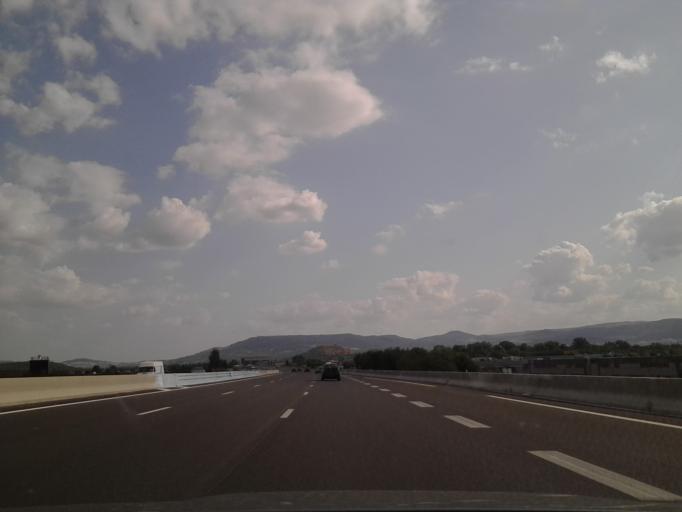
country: FR
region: Auvergne
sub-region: Departement du Puy-de-Dome
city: Aulnat
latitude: 45.8020
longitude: 3.1490
